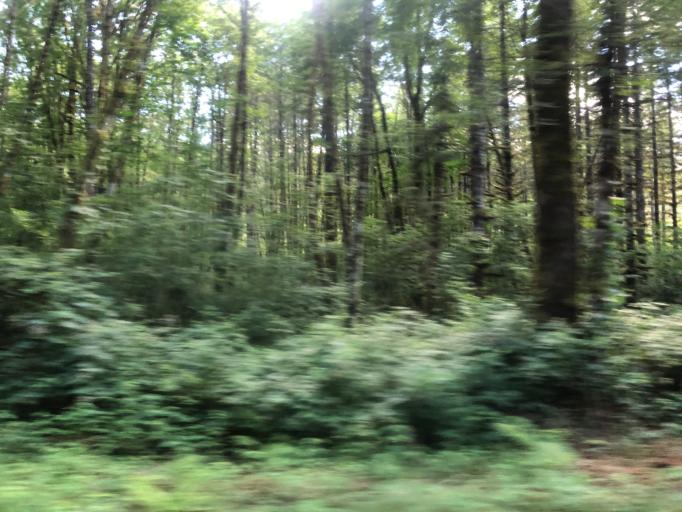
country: US
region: Oregon
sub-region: Clackamas County
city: Sandy
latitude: 45.4283
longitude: -122.2296
